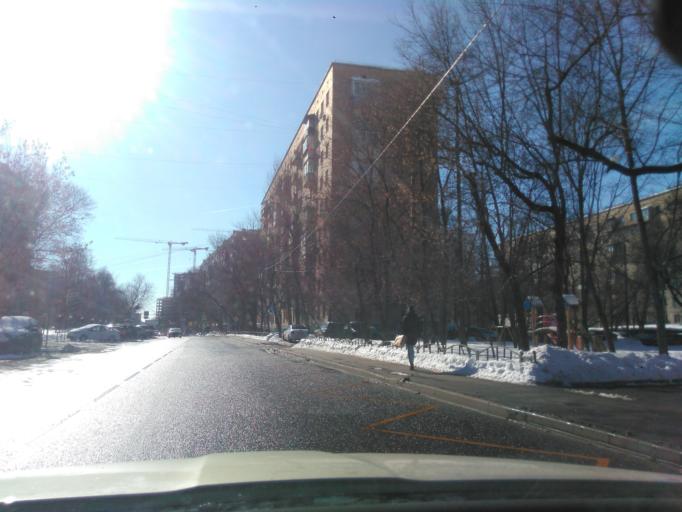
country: RU
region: Moskovskaya
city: Dorogomilovo
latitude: 55.7956
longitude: 37.5687
